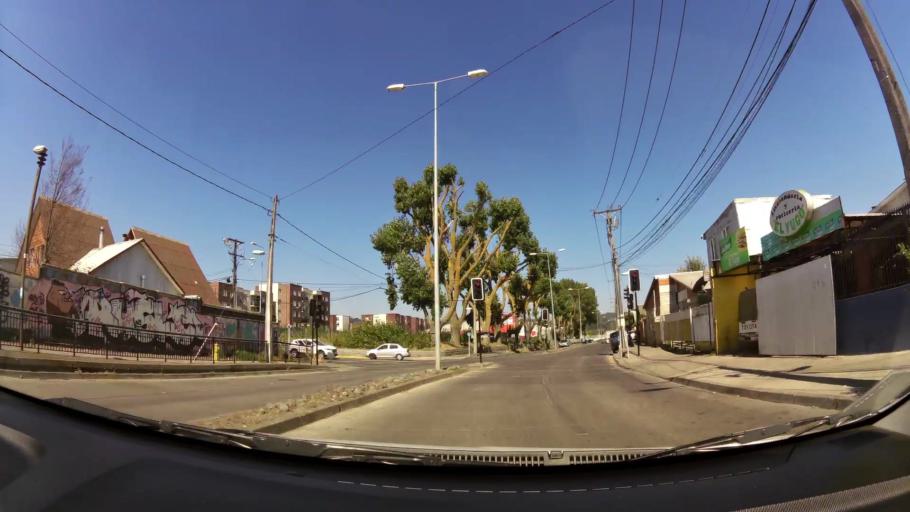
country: CL
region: Biobio
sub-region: Provincia de Concepcion
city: Concepcion
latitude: -36.7925
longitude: -73.0373
